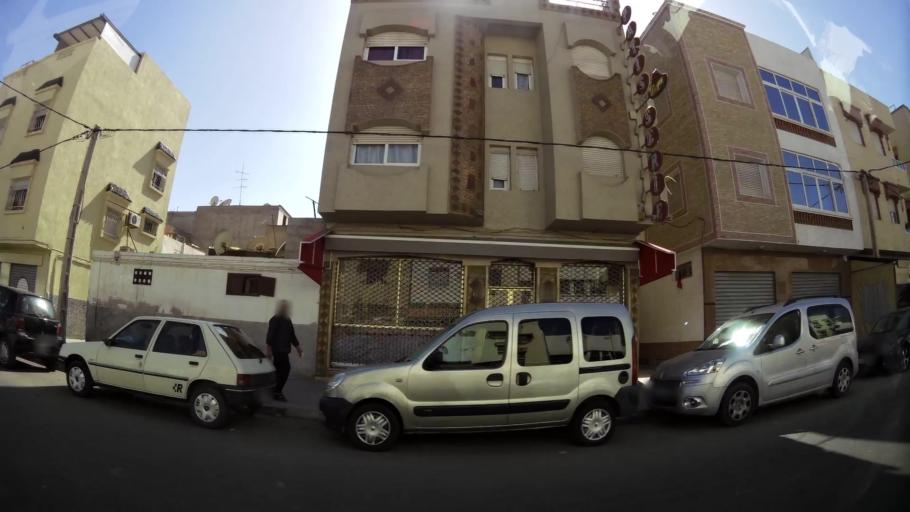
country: MA
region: Souss-Massa-Draa
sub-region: Agadir-Ida-ou-Tnan
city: Agadir
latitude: 30.4114
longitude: -9.5877
